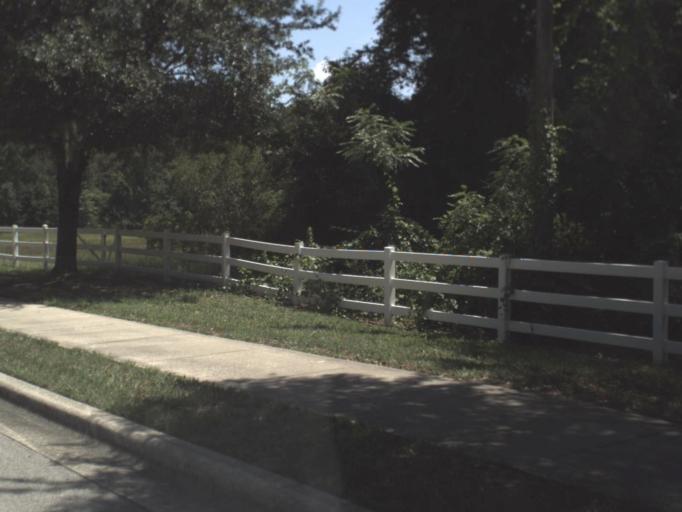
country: US
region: Florida
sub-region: Saint Johns County
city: Fruit Cove
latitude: 30.1105
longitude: -81.6263
